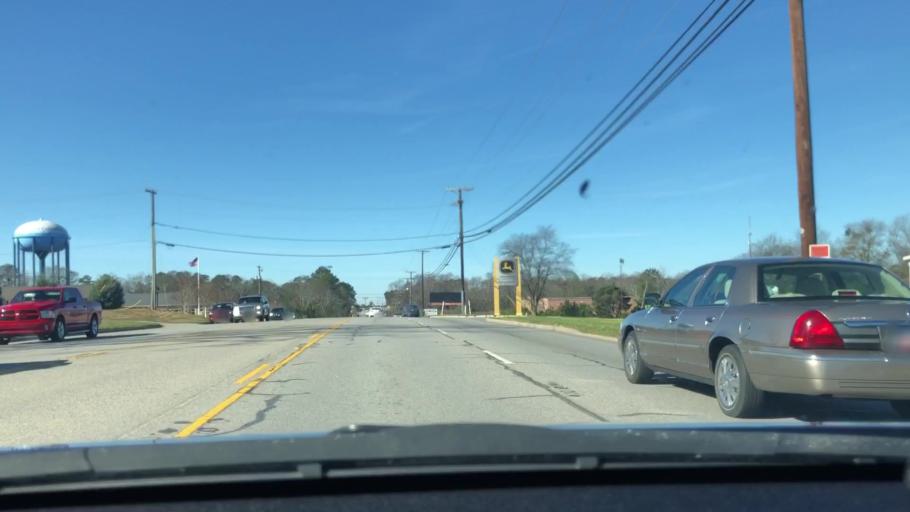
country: US
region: South Carolina
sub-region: Lexington County
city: Oak Grove
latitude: 34.0080
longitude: -81.1316
